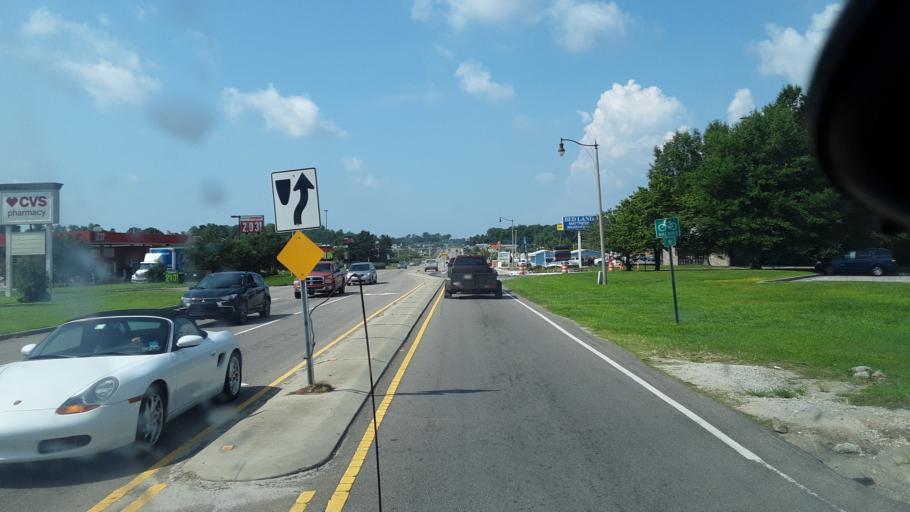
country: US
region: North Carolina
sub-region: Brunswick County
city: Shallotte
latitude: 33.9814
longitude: -78.3736
